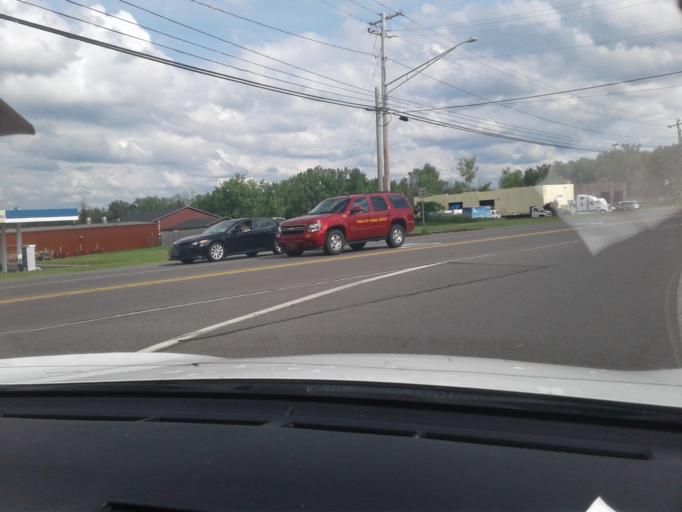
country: US
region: New York
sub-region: Onondaga County
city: East Syracuse
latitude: 43.0929
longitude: -76.0595
